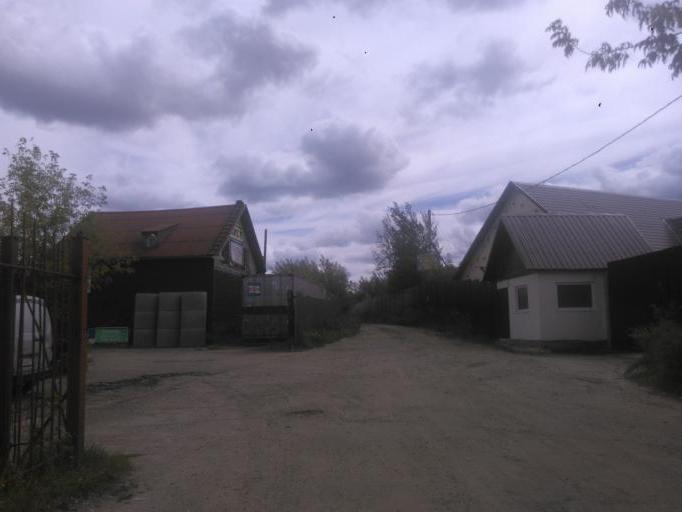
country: RU
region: Moskovskaya
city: Solnechnogorsk
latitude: 56.1468
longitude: 36.9174
